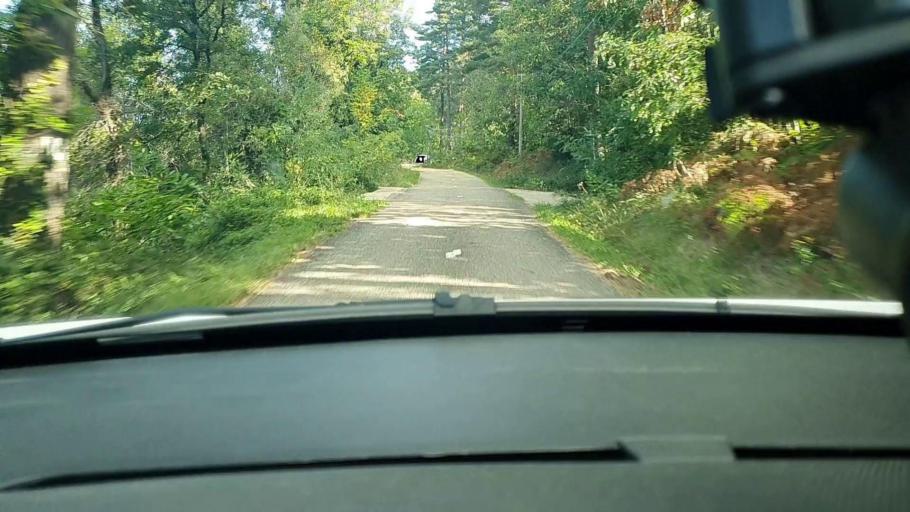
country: FR
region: Languedoc-Roussillon
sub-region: Departement du Gard
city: Besseges
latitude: 44.3855
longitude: 3.9914
